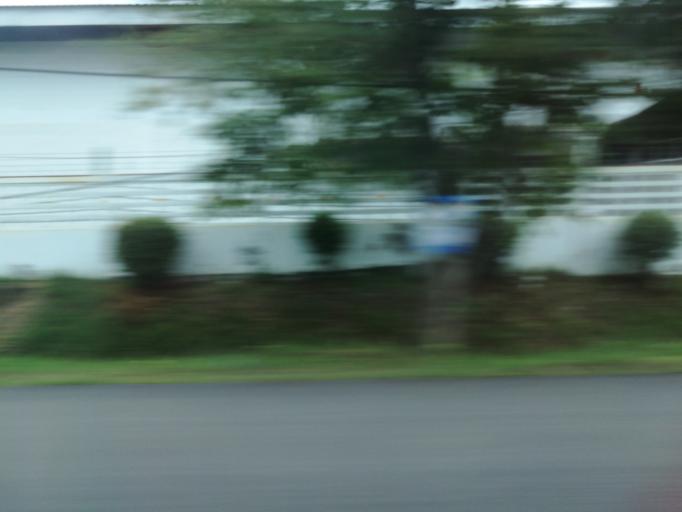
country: TH
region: Prachuap Khiri Khan
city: Prachuap Khiri Khan
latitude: 11.8744
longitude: 99.7868
